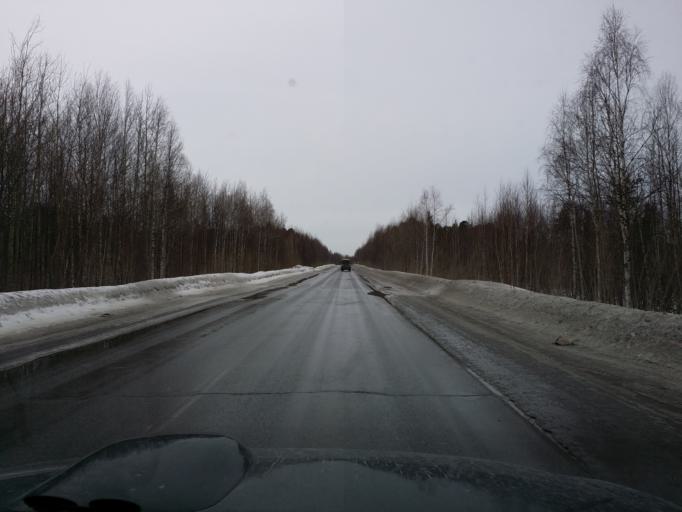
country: RU
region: Tomsk
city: Strezhevoy
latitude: 60.7440
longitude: 77.5252
